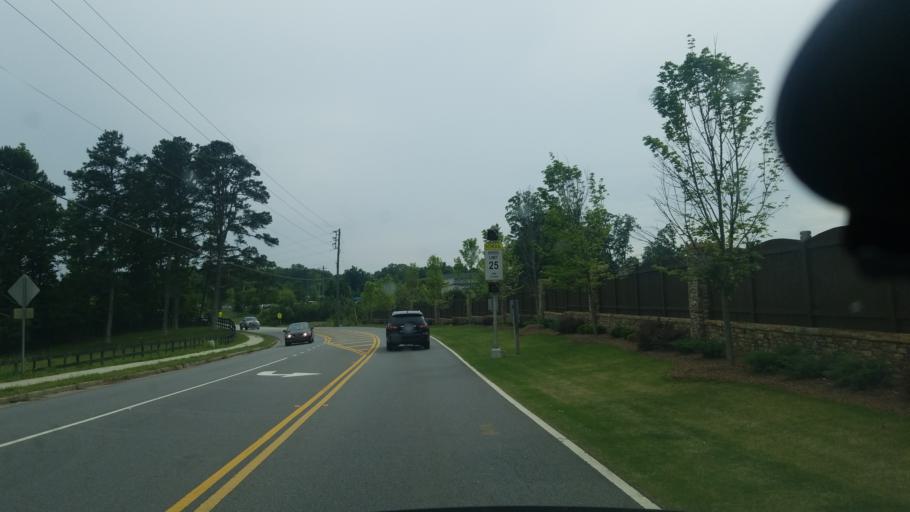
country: US
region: Georgia
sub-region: Gwinnett County
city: Suwanee
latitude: 34.1095
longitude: -84.1405
